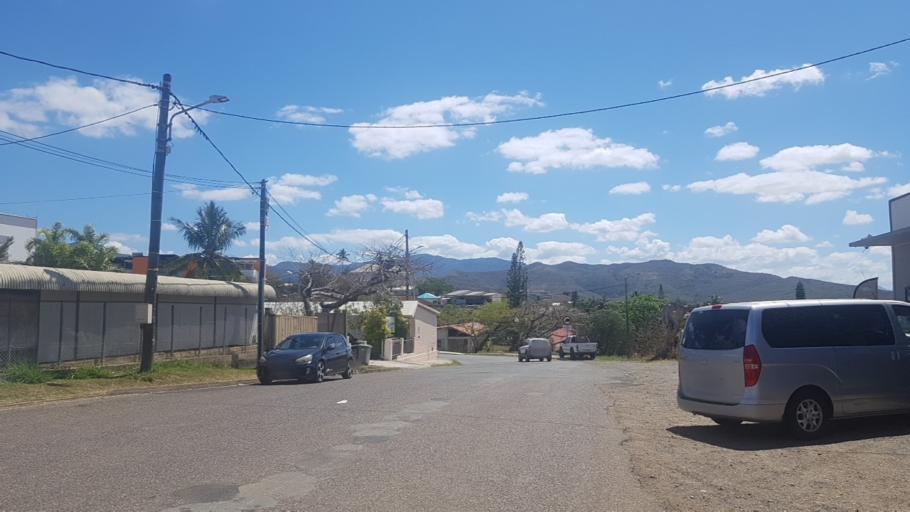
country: NC
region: North Province
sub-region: Kone
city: Kone
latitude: -21.0613
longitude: 164.8623
